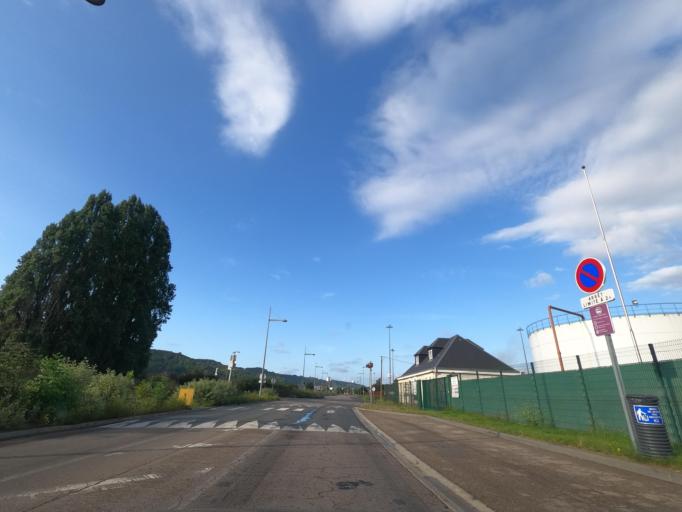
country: FR
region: Haute-Normandie
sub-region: Departement de la Seine-Maritime
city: Petit-Couronne
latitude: 49.4116
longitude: 1.0181
